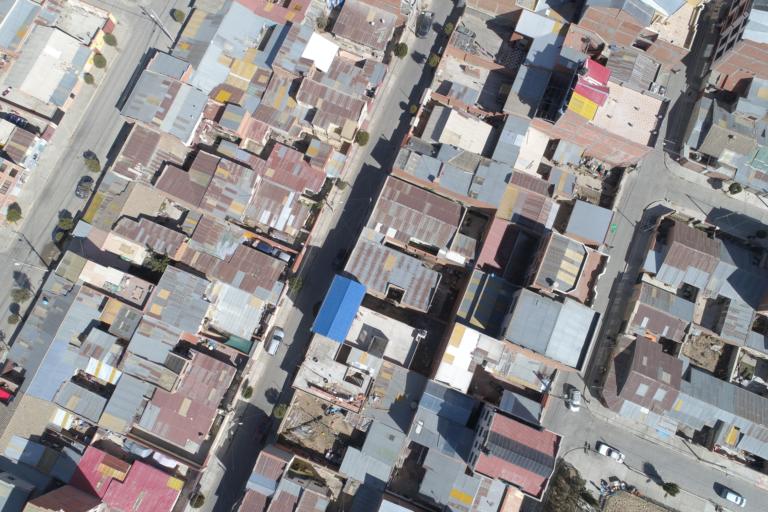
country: BO
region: La Paz
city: La Paz
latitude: -16.5306
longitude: -68.1559
